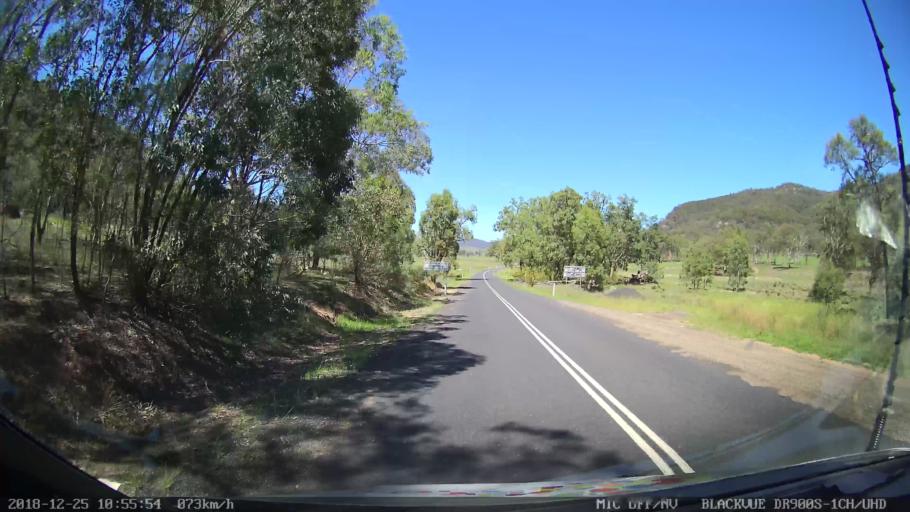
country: AU
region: New South Wales
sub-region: Upper Hunter Shire
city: Merriwa
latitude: -32.3986
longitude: 150.2686
